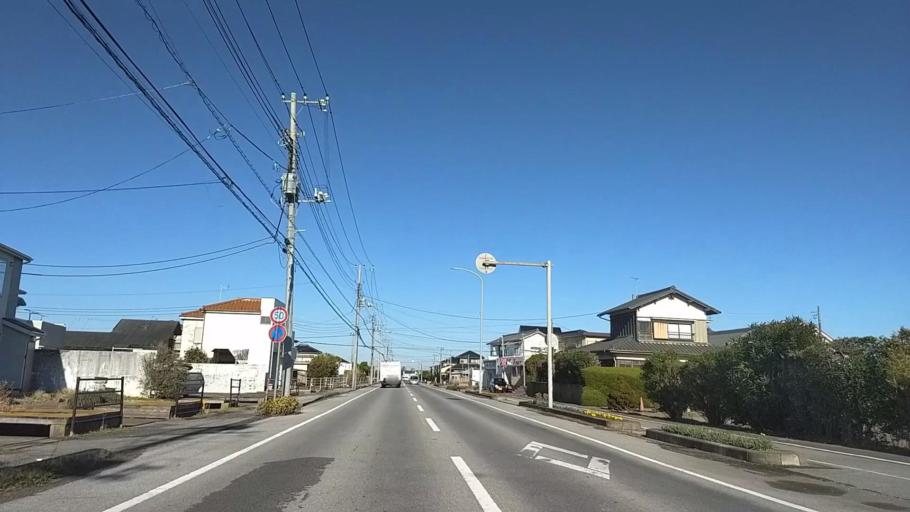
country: JP
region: Chiba
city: Togane
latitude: 35.5109
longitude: 140.4358
